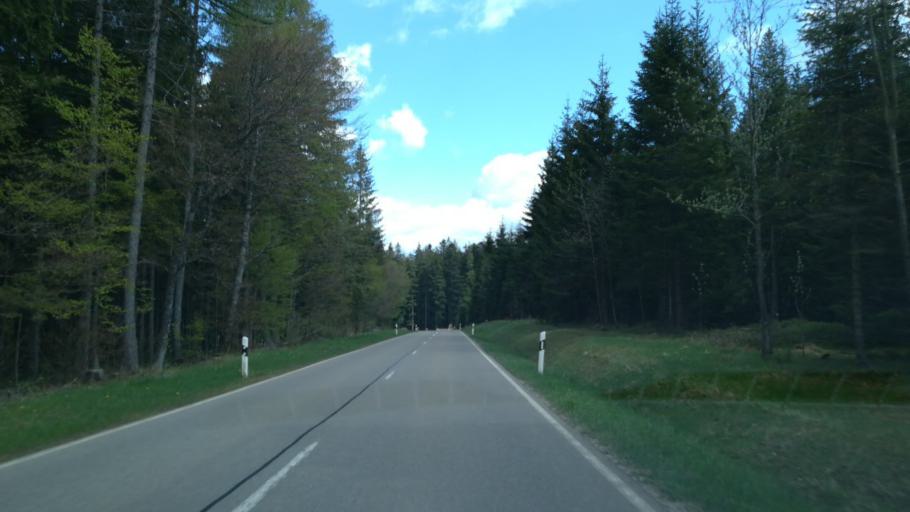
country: DE
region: Baden-Wuerttemberg
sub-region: Freiburg Region
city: Lenzkirch
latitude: 47.8301
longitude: 8.2419
